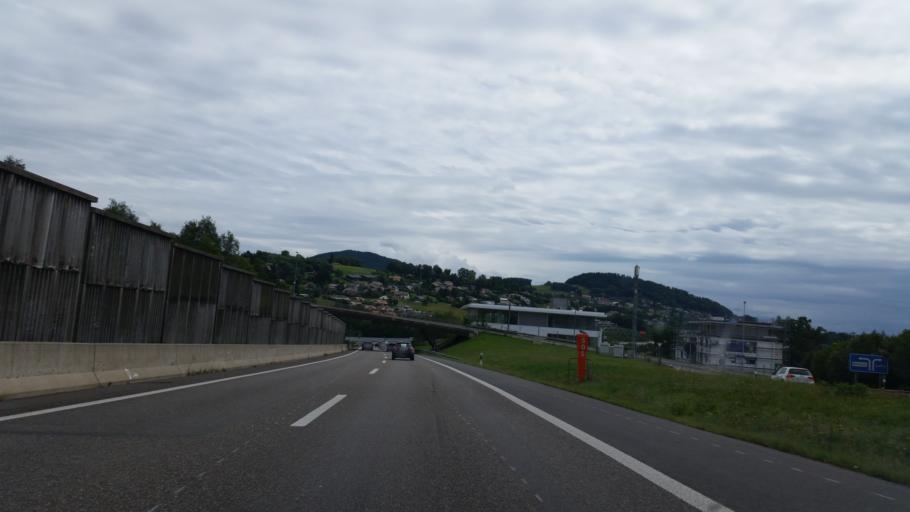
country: CH
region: Vaud
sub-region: Lavaux-Oron District
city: Belmont-sur-Lausanne
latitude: 46.5171
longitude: 6.6901
